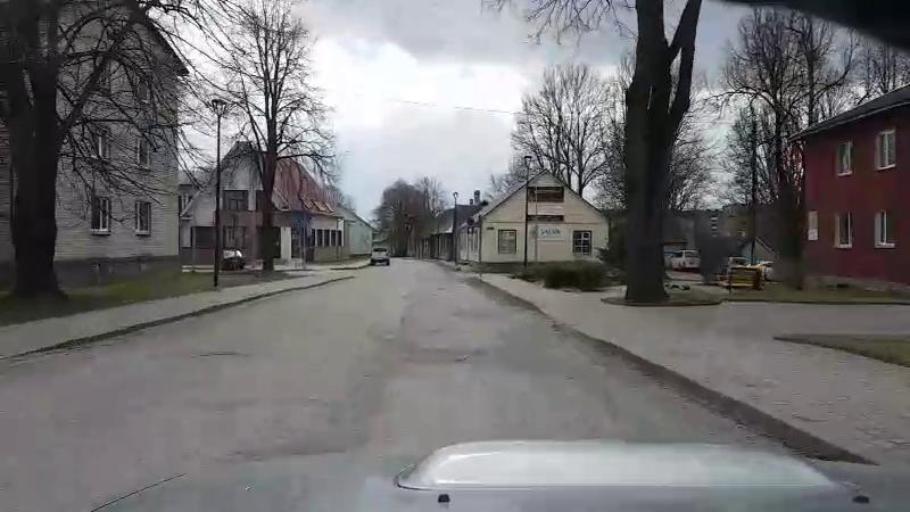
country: EE
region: Jaervamaa
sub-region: Paide linn
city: Paide
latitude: 58.8860
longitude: 25.5704
